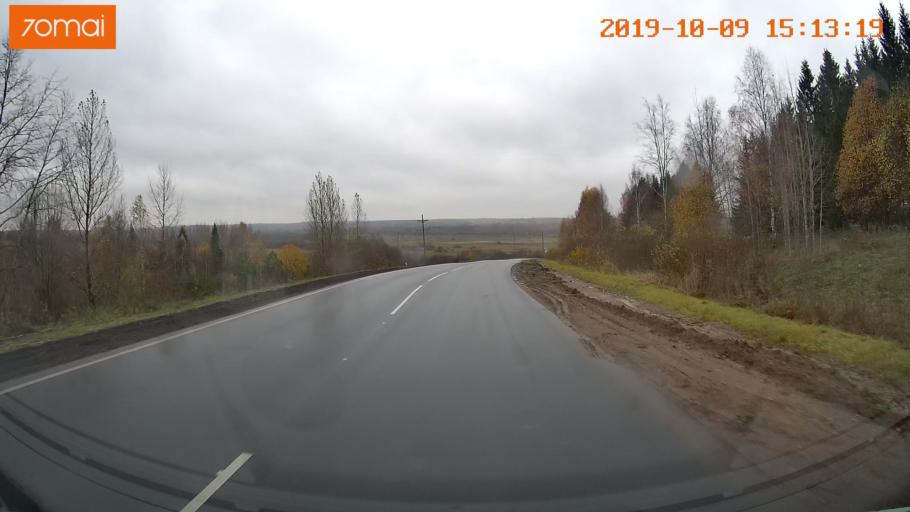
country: RU
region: Kostroma
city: Susanino
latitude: 58.1473
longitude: 41.6152
